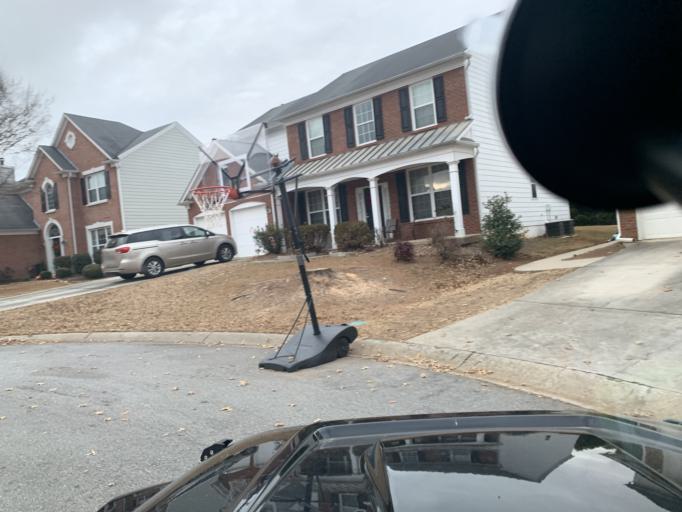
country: US
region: Georgia
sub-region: Cherokee County
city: Woodstock
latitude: 34.0975
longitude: -84.4582
